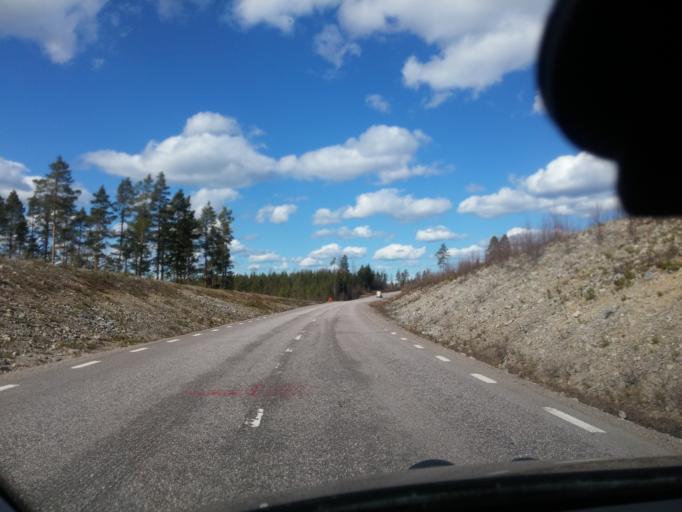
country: SE
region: Gaevleborg
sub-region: Ovanakers Kommun
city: Edsbyn
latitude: 61.2343
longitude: 15.8822
